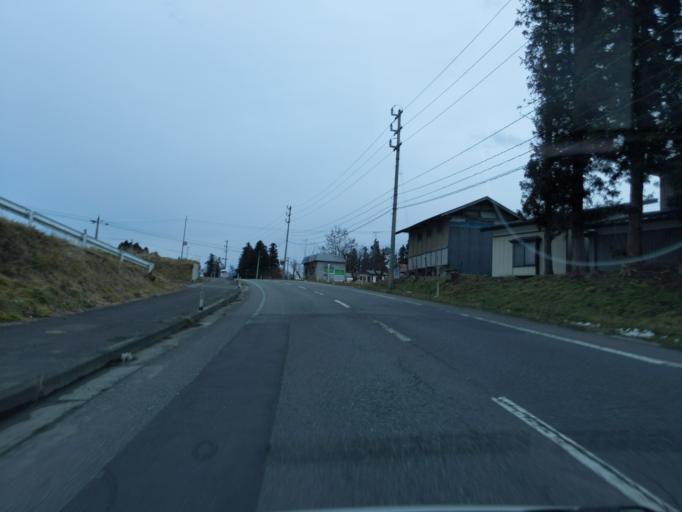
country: JP
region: Iwate
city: Ichinoseki
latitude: 39.0238
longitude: 141.3219
